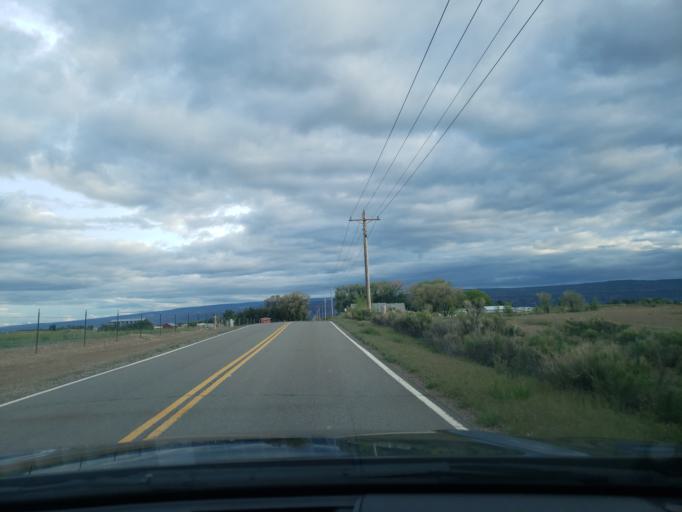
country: US
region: Colorado
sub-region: Mesa County
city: Fruita
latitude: 39.2208
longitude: -108.7011
